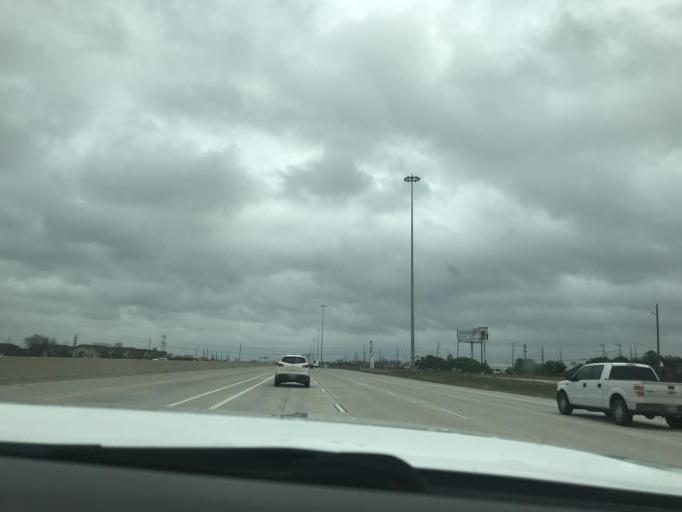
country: US
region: Texas
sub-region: Fort Bend County
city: Greatwood
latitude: 29.5591
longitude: -95.7002
